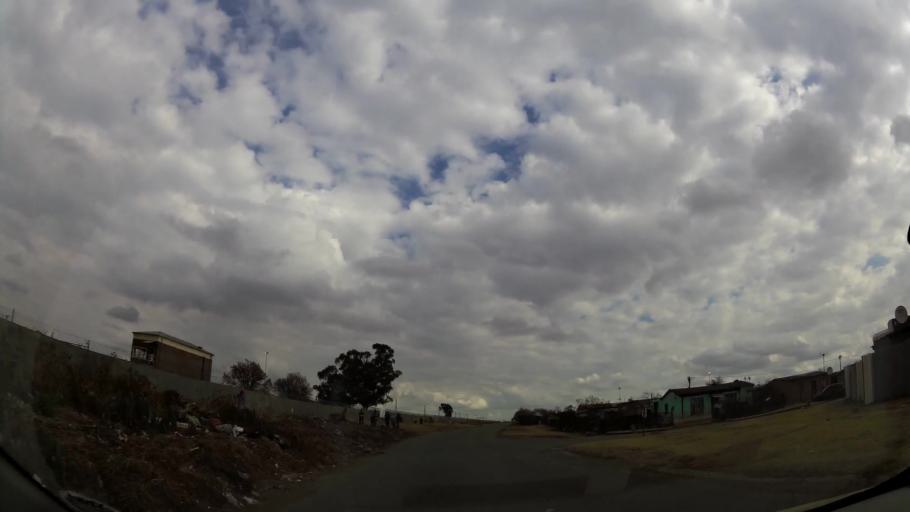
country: ZA
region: Orange Free State
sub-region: Fezile Dabi District Municipality
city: Sasolburg
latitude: -26.8556
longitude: 27.8633
